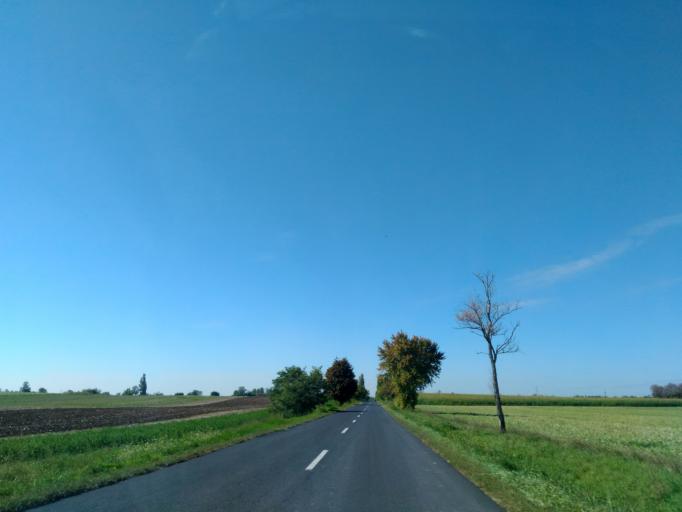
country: HU
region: Fejer
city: Ivancsa
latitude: 47.1777
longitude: 18.8192
